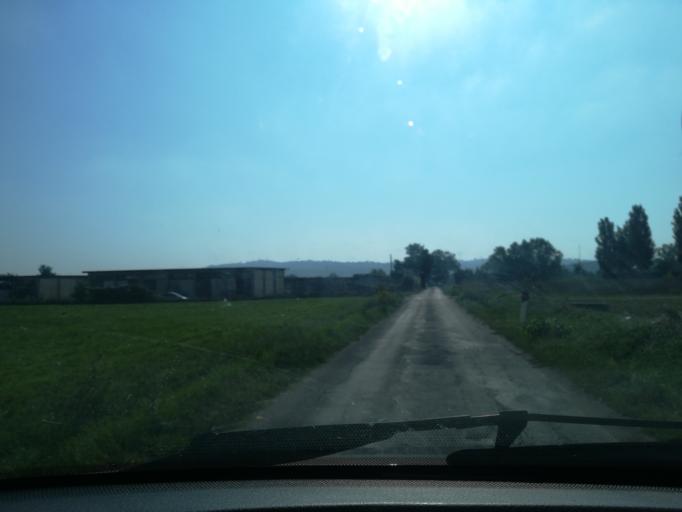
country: IT
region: The Marches
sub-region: Provincia di Macerata
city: Piediripa
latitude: 43.2730
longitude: 13.4677
